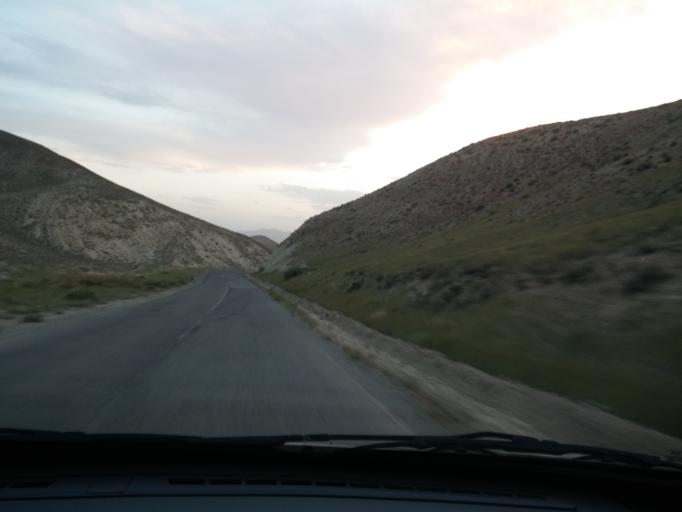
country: IR
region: Tehran
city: Damavand
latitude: 35.5368
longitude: 52.3049
